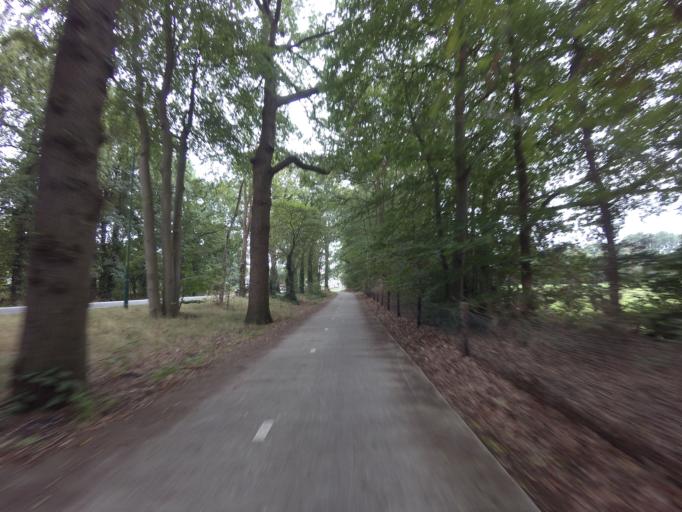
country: NL
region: North Holland
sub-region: Gemeente Wijdemeren
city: Nieuw-Loosdrecht
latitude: 52.1800
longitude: 5.1770
